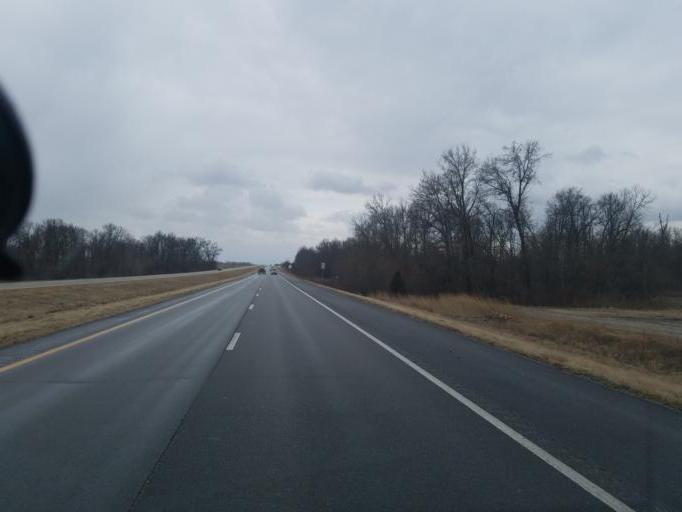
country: US
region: Missouri
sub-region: Randolph County
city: Moberly
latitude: 39.3523
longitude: -92.3974
